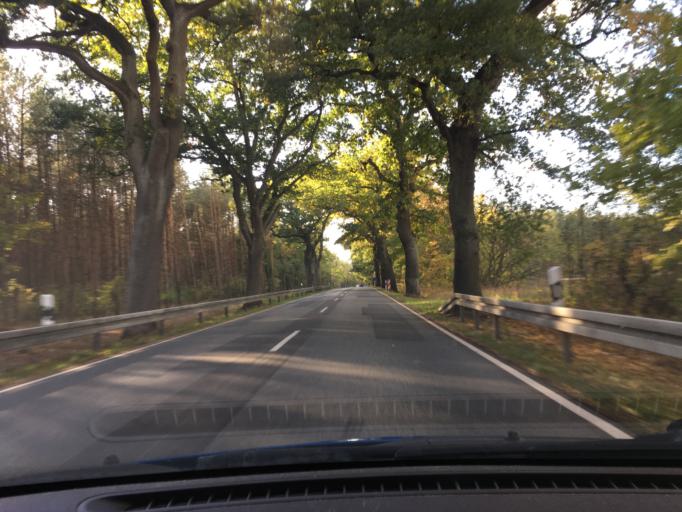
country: DE
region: Mecklenburg-Vorpommern
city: Boizenburg
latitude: 53.3874
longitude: 10.8374
